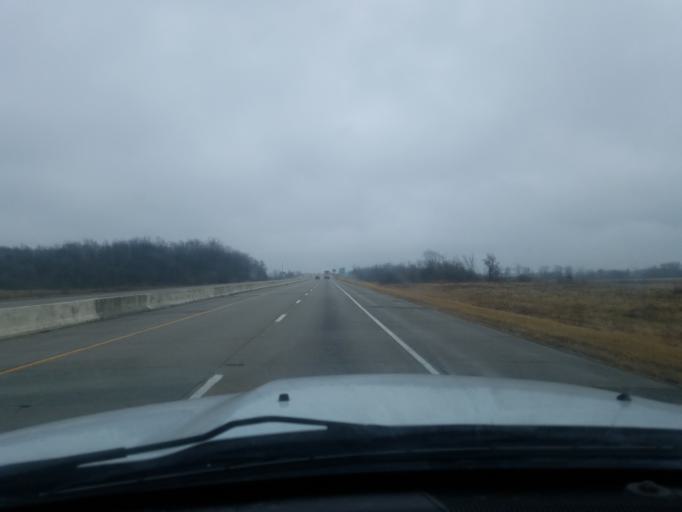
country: US
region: Indiana
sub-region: Wells County
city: Ossian
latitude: 40.9531
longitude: -85.1871
